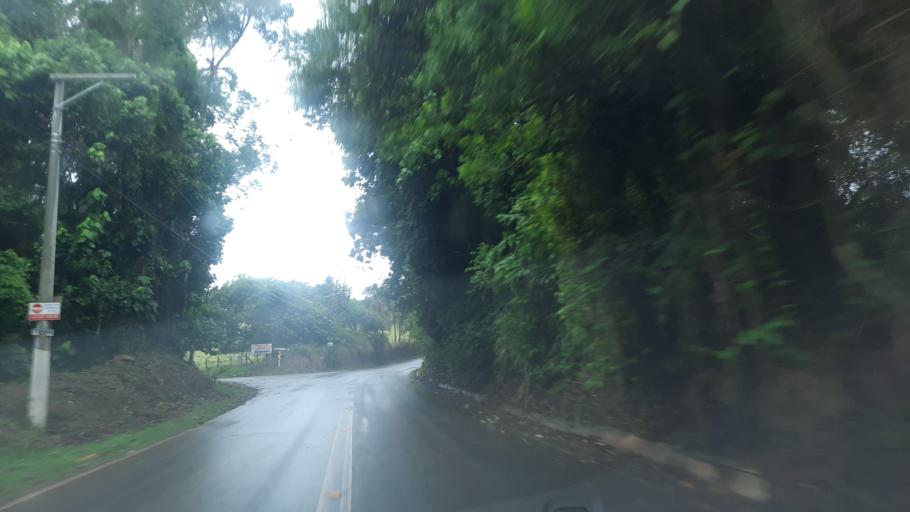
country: BR
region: Sao Paulo
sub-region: Atibaia
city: Atibaia
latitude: -23.0804
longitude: -46.5251
